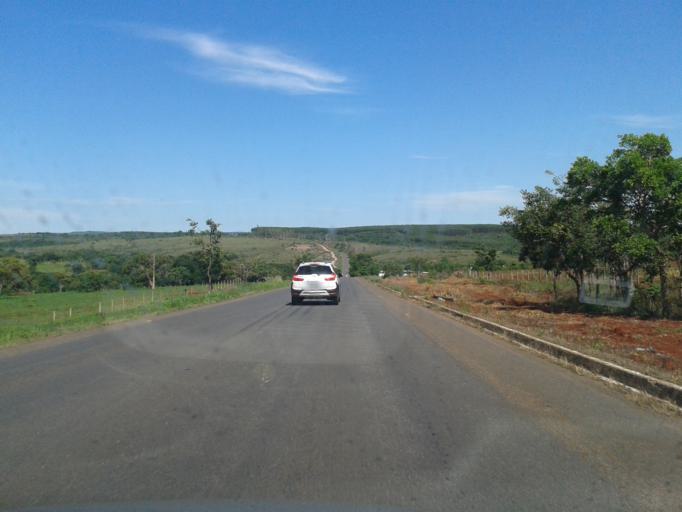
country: BR
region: Goias
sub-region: Bela Vista De Goias
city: Bela Vista de Goias
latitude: -17.1770
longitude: -48.7201
